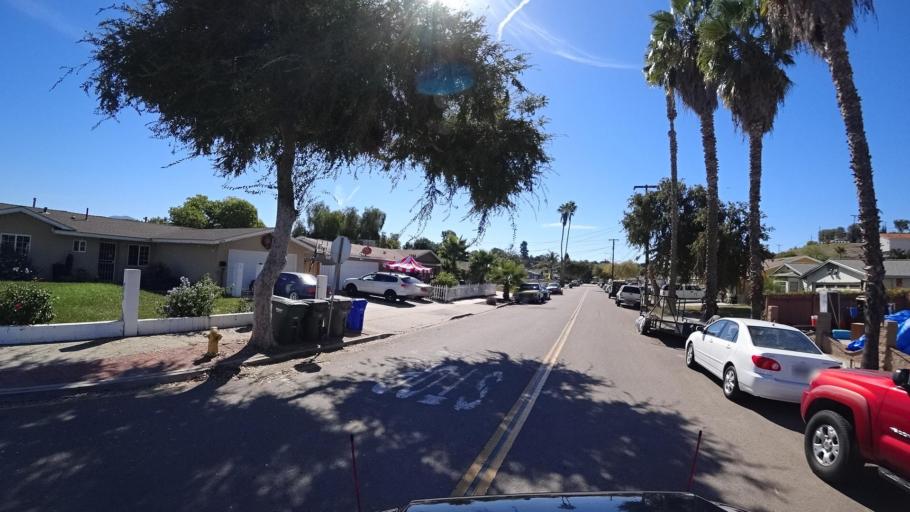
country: US
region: California
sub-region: San Diego County
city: Lemon Grove
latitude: 32.7248
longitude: -117.0220
